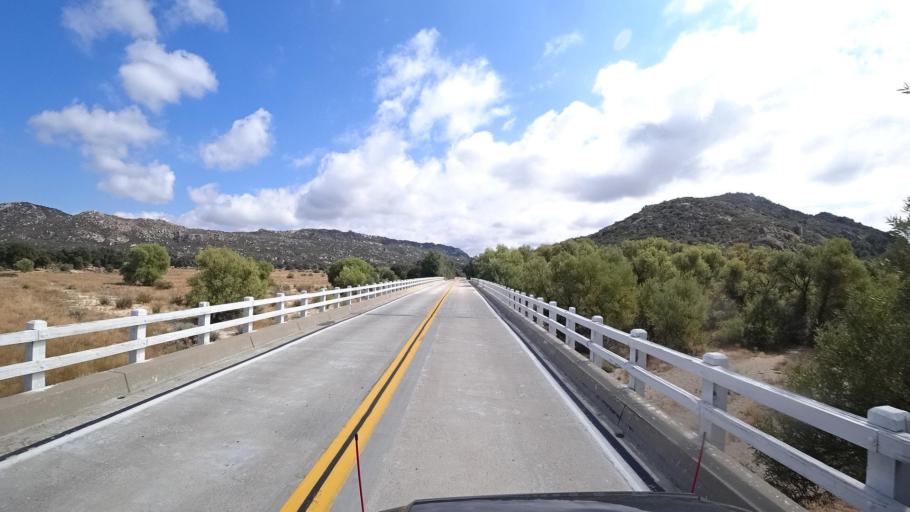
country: US
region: California
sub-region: San Diego County
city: Pine Valley
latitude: 32.7153
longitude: -116.4993
